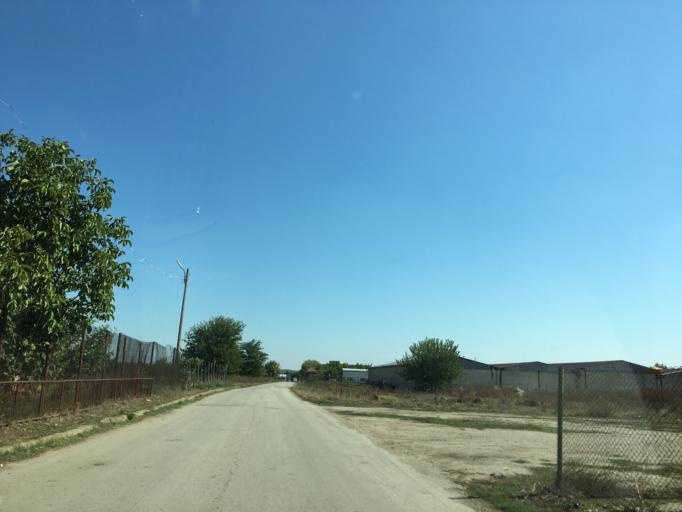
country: BG
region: Pleven
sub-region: Obshtina Knezha
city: Knezha
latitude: 43.5138
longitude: 24.0867
